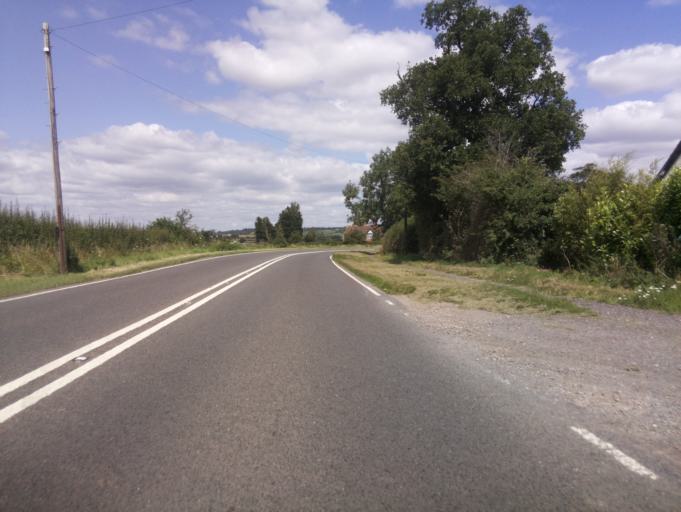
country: GB
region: England
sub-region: Buckinghamshire
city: Aylesbury
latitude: 51.8564
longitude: -0.8295
